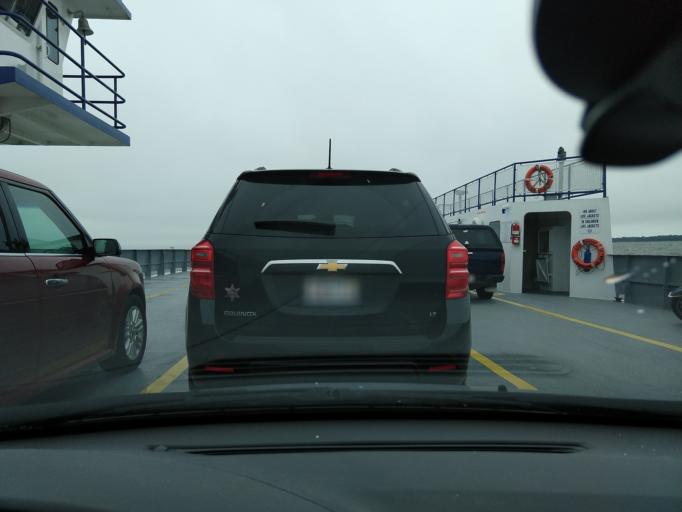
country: US
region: Alabama
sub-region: Mobile County
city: Dauphin Island
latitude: 30.2408
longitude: -88.0220
